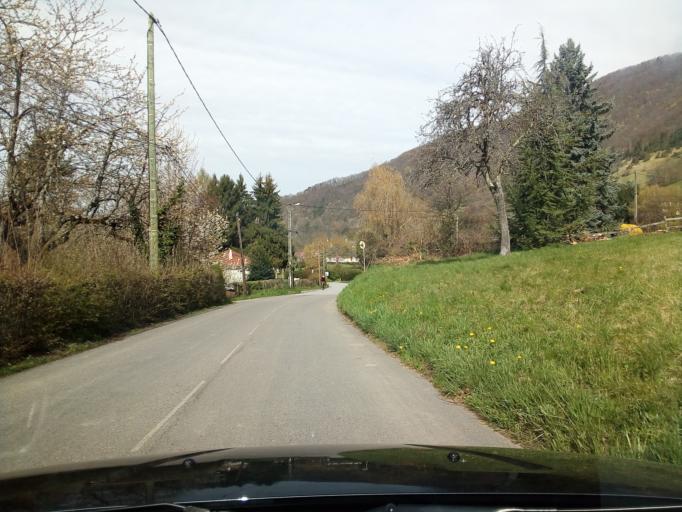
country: FR
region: Rhone-Alpes
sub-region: Departement de l'Isere
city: Revel
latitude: 45.1637
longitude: 5.8371
